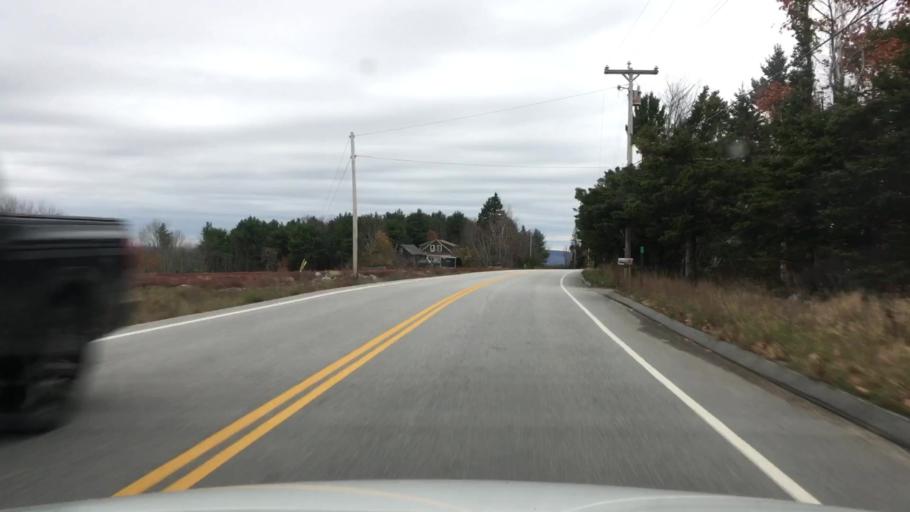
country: US
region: Maine
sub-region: Hancock County
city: Orland
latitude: 44.5327
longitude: -68.6764
